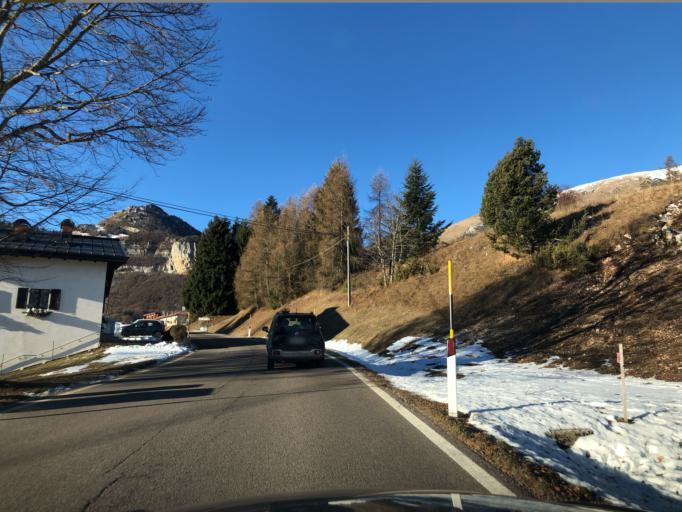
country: IT
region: Trentino-Alto Adige
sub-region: Provincia di Trento
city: Brentonico
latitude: 45.8003
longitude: 10.9239
